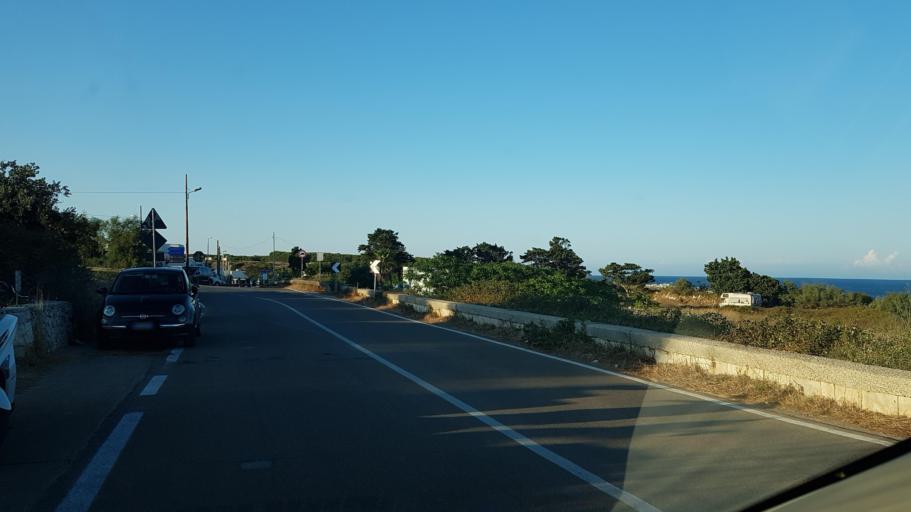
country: IT
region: Apulia
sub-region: Provincia di Lecce
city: Uggiano la Chiesa
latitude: 40.0774
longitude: 18.4815
